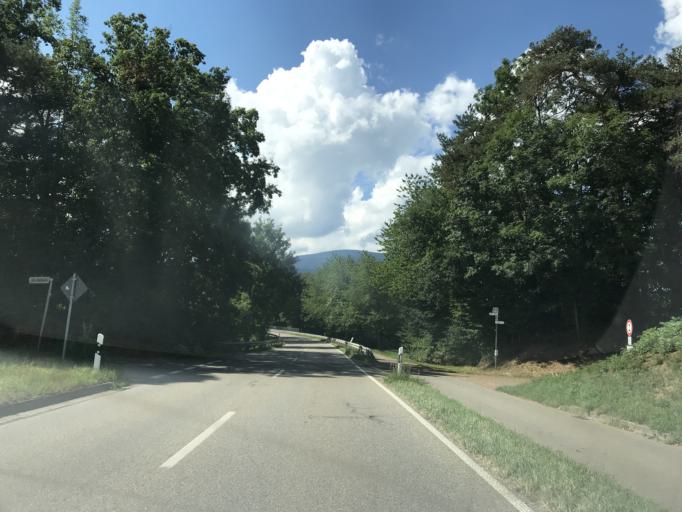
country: DE
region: Baden-Wuerttemberg
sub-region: Freiburg Region
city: Stegen
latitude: 47.9755
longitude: 7.9605
